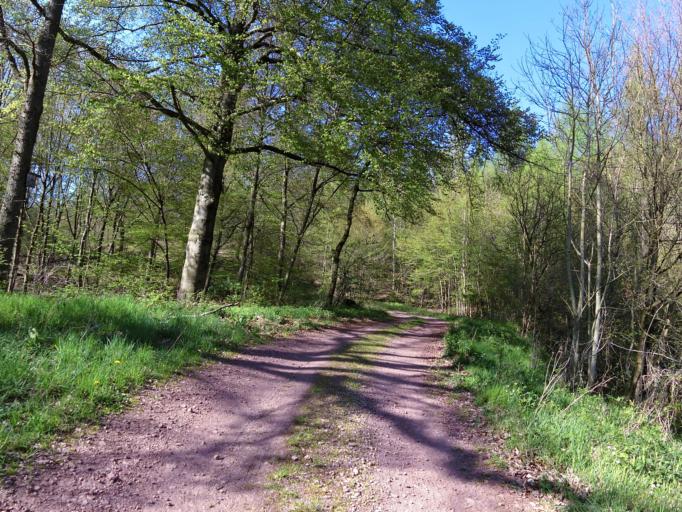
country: DE
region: Thuringia
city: Wolfsburg-Unkeroda
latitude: 50.9363
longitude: 10.2721
